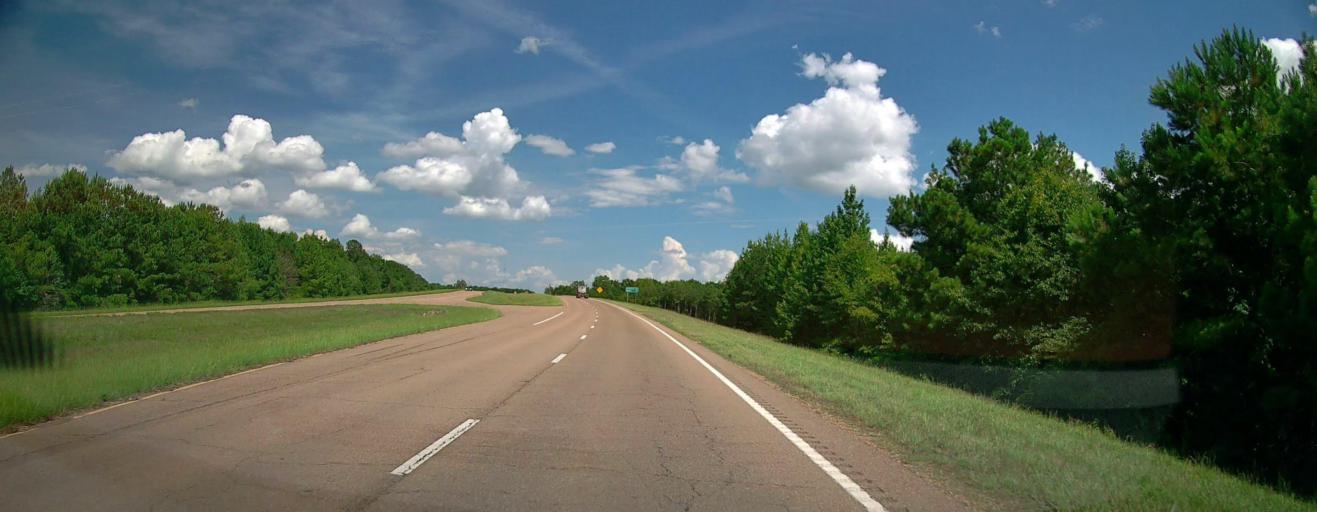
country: US
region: Mississippi
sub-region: Monroe County
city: Aberdeen
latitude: 33.8095
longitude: -88.4838
